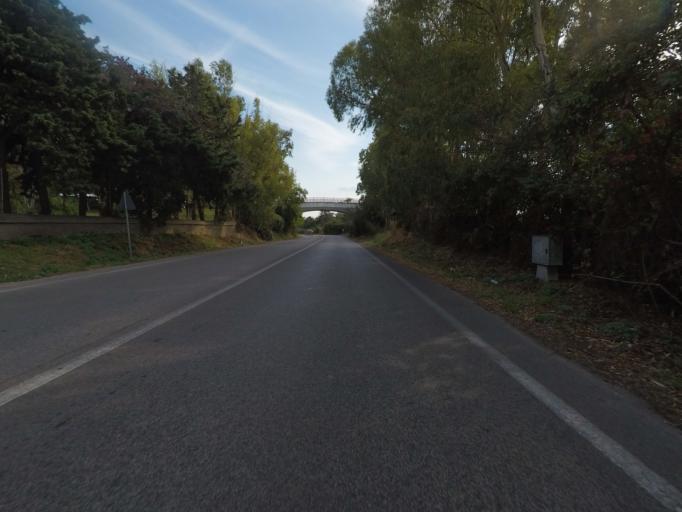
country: IT
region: Latium
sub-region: Citta metropolitana di Roma Capitale
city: Civitavecchia
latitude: 42.0599
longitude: 11.8170
